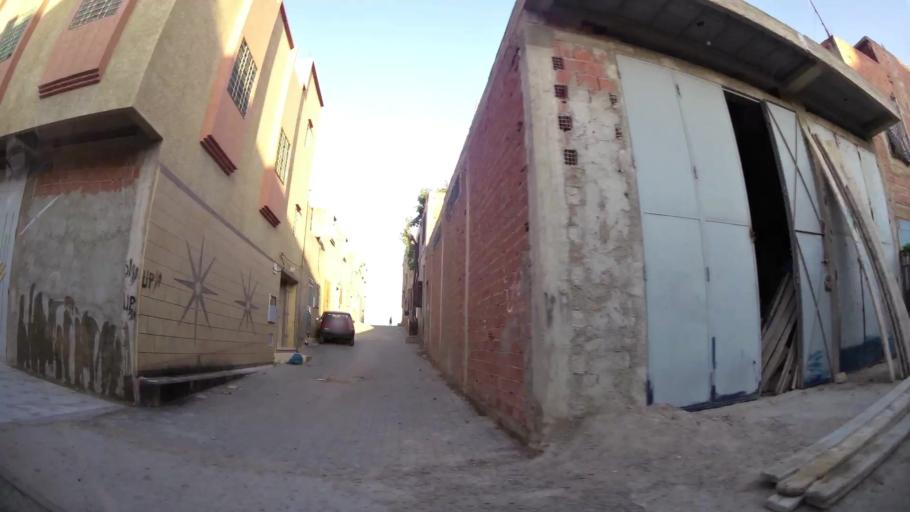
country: MA
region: Oriental
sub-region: Oujda-Angad
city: Oujda
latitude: 34.7097
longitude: -1.9076
